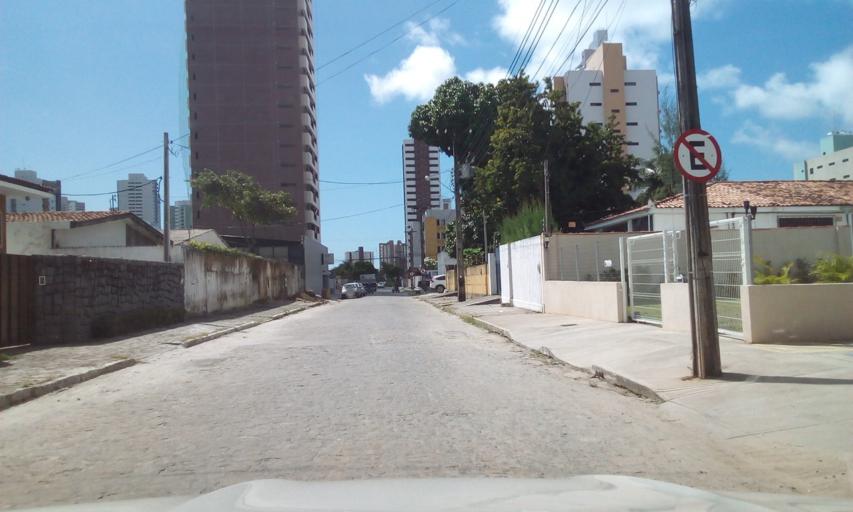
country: BR
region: Paraiba
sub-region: Joao Pessoa
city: Joao Pessoa
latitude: -7.1204
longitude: -34.8439
